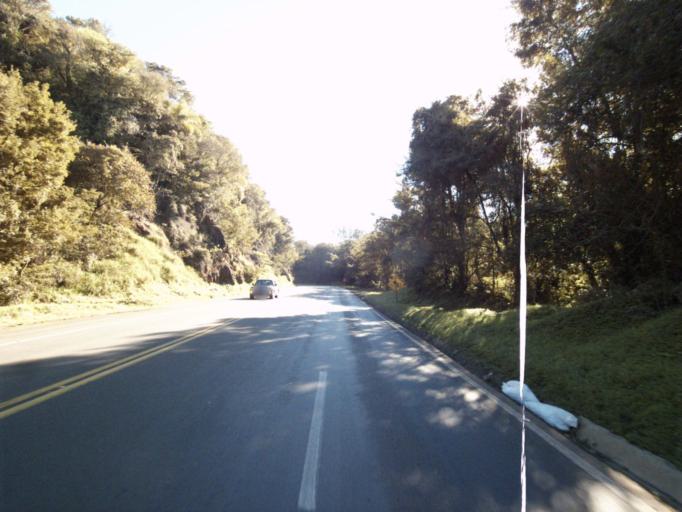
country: BR
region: Santa Catarina
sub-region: Chapeco
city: Chapeco
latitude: -26.9954
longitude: -52.6251
